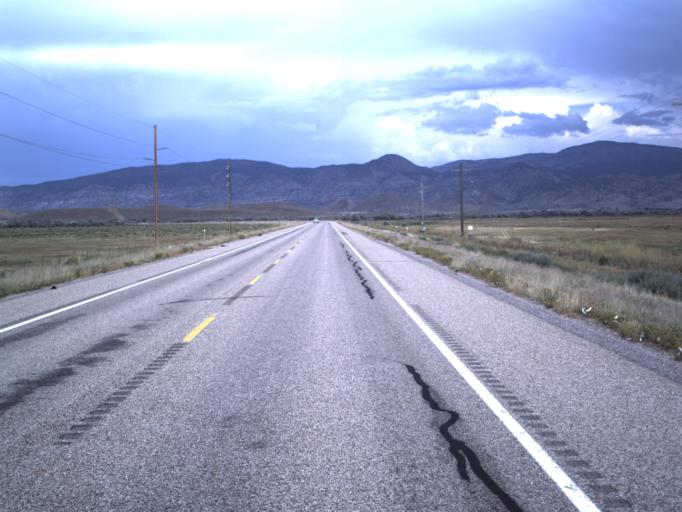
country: US
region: Utah
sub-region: Piute County
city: Junction
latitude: 38.1876
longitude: -112.2402
